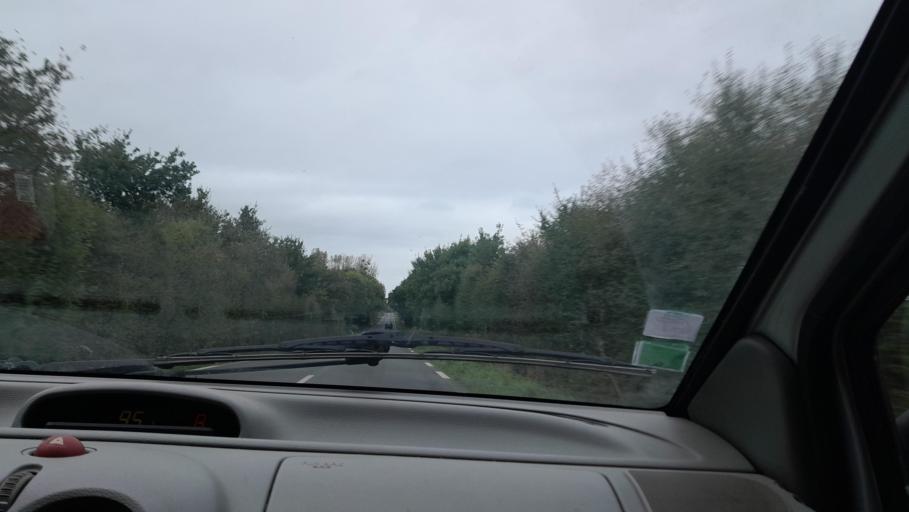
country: FR
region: Pays de la Loire
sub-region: Departement de Maine-et-Loire
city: Pouance
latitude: 47.6437
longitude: -1.2017
